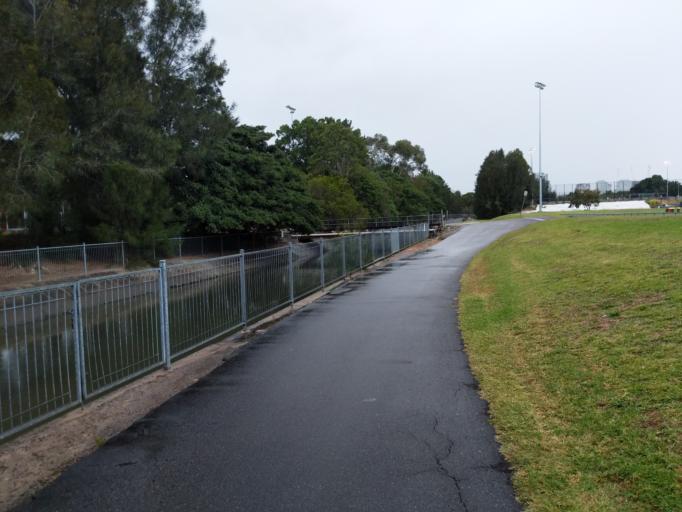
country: AU
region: New South Wales
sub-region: Canada Bay
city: Concord
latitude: -33.8646
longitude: 151.1120
